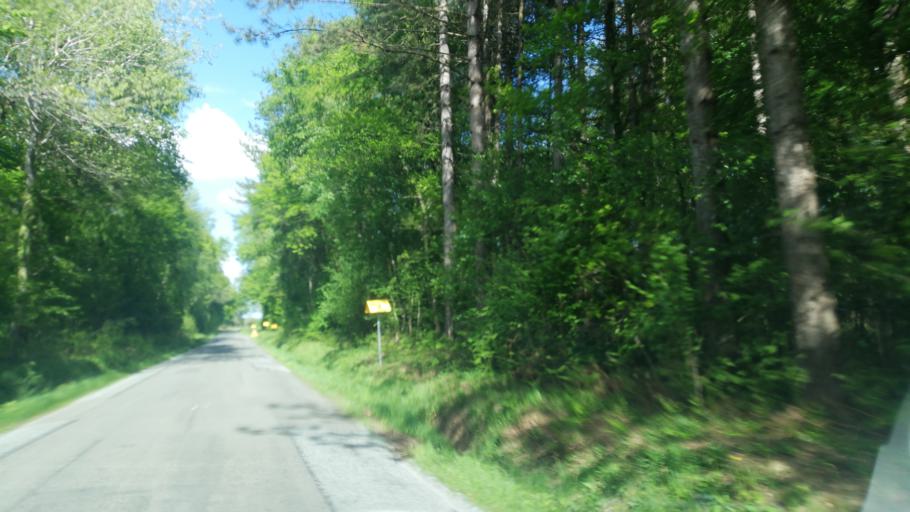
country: FR
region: Brittany
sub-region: Departement d'Ille-et-Vilaine
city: Montauban-de-Bretagne
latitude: 48.2164
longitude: -2.0157
